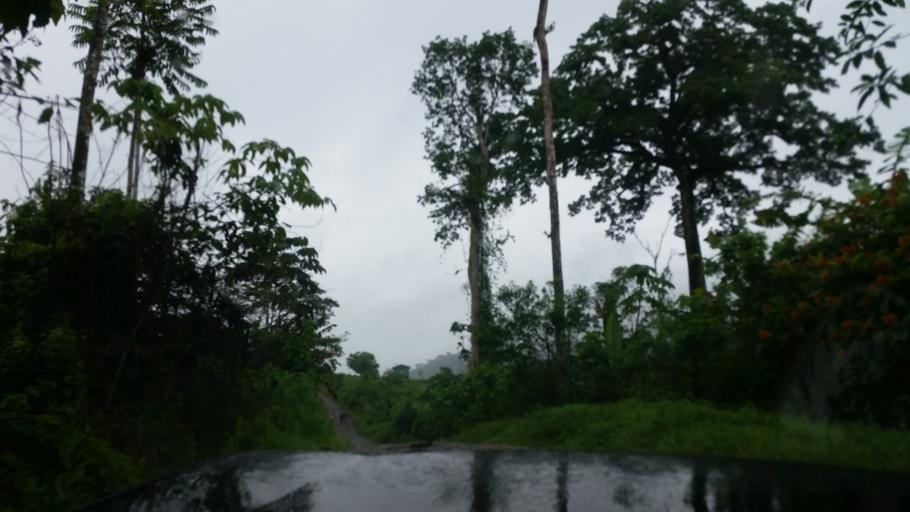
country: NI
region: Atlantico Norte (RAAN)
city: Bonanza
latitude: 14.0817
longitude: -84.6767
